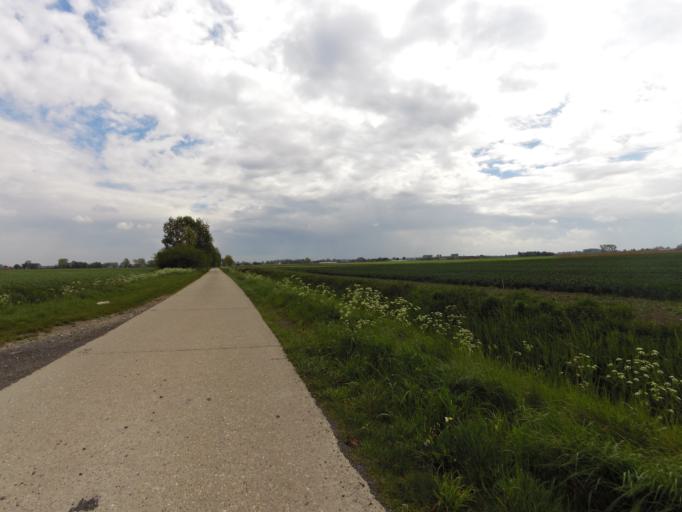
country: BE
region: Flanders
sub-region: Provincie West-Vlaanderen
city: Koekelare
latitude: 51.1103
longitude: 2.9128
